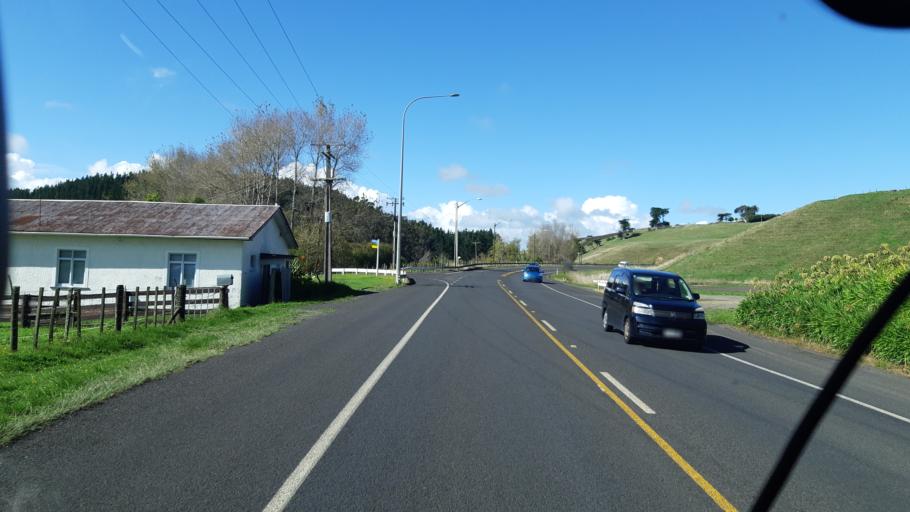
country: NZ
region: Manawatu-Wanganui
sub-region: Wanganui District
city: Wanganui
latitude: -39.9608
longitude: 175.0969
